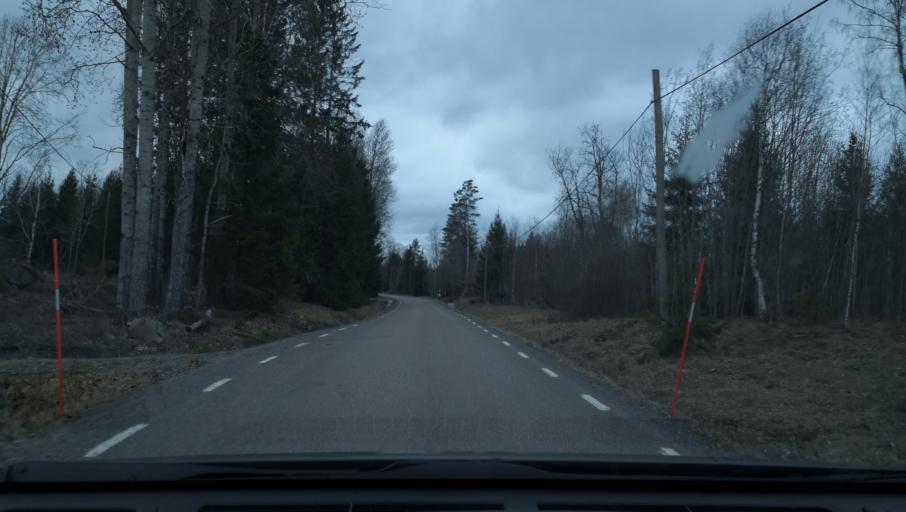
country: SE
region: Vaestmanland
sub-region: Kopings Kommun
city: Kolsva
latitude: 59.5640
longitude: 15.7359
